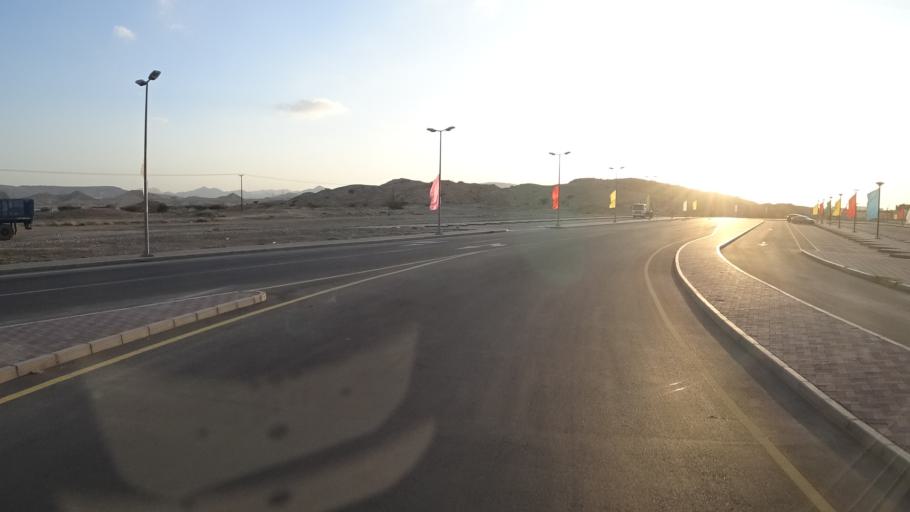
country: OM
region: Muhafazat Masqat
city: As Sib al Jadidah
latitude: 23.5849
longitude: 58.2031
